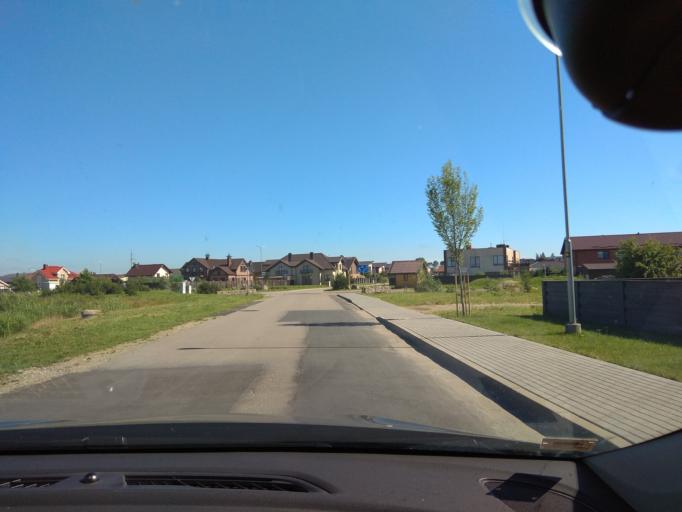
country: LT
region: Klaipedos apskritis
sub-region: Klaipeda
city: Klaipeda
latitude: 55.7498
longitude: 21.1783
